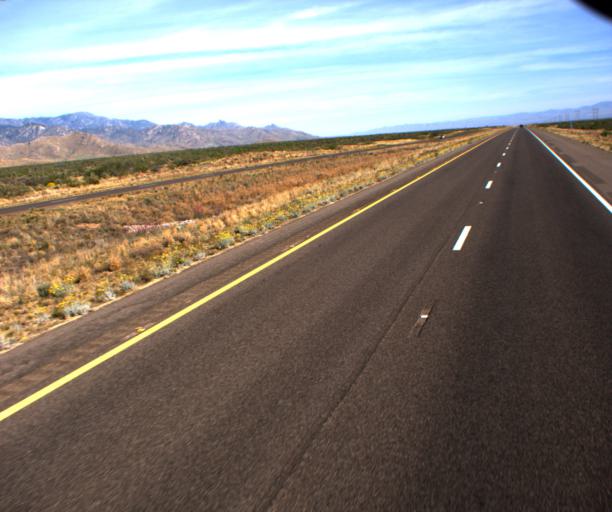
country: US
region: Arizona
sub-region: Graham County
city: Swift Trail Junction
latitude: 32.5483
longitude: -109.6771
